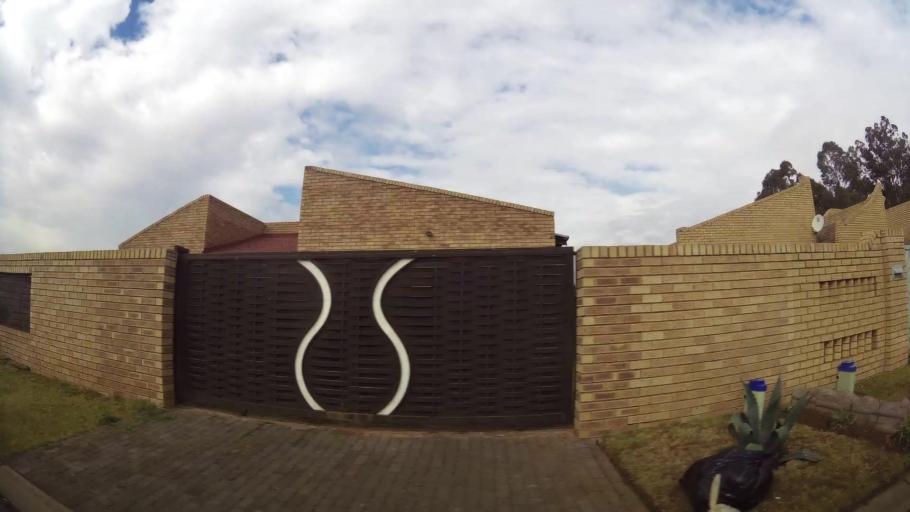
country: ZA
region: Gauteng
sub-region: Ekurhuleni Metropolitan Municipality
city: Germiston
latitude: -26.3275
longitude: 28.1796
